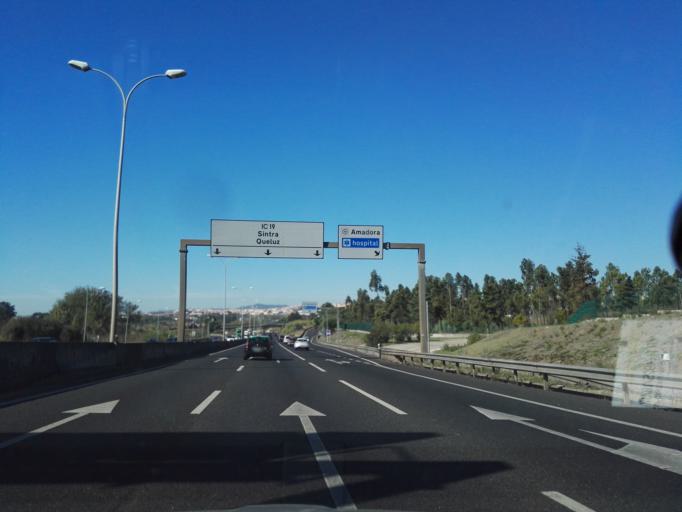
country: PT
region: Lisbon
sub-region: Amadora
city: Amadora
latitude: 38.7478
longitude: -9.2421
